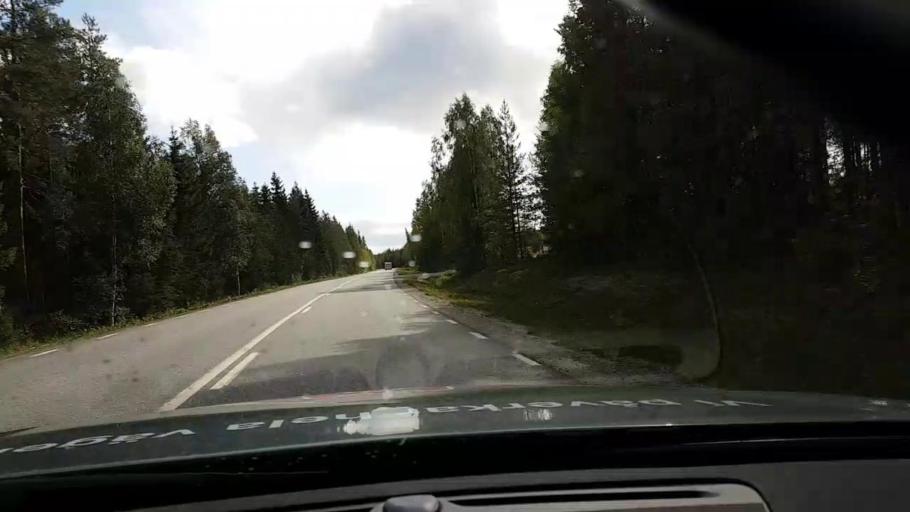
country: SE
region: Vaesternorrland
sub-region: OErnskoeldsviks Kommun
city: Bredbyn
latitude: 63.6290
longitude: 17.9106
